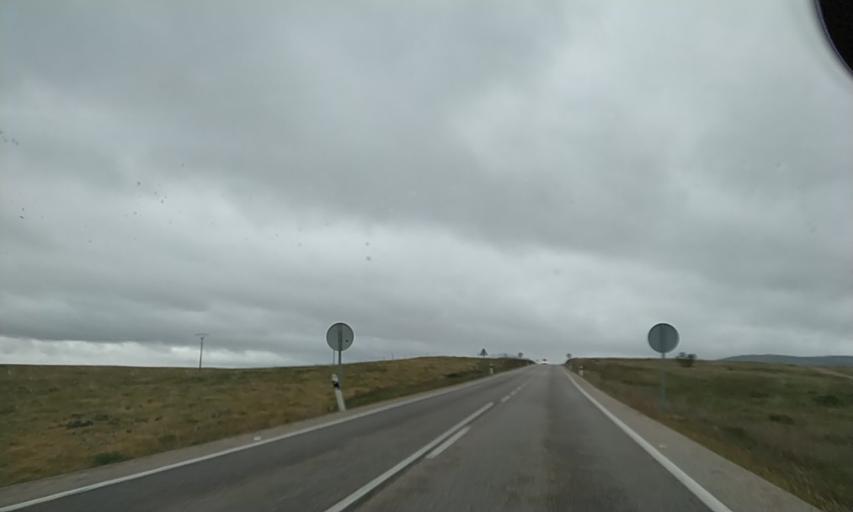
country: ES
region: Extremadura
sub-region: Provincia de Caceres
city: Caceres
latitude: 39.5170
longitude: -6.3973
